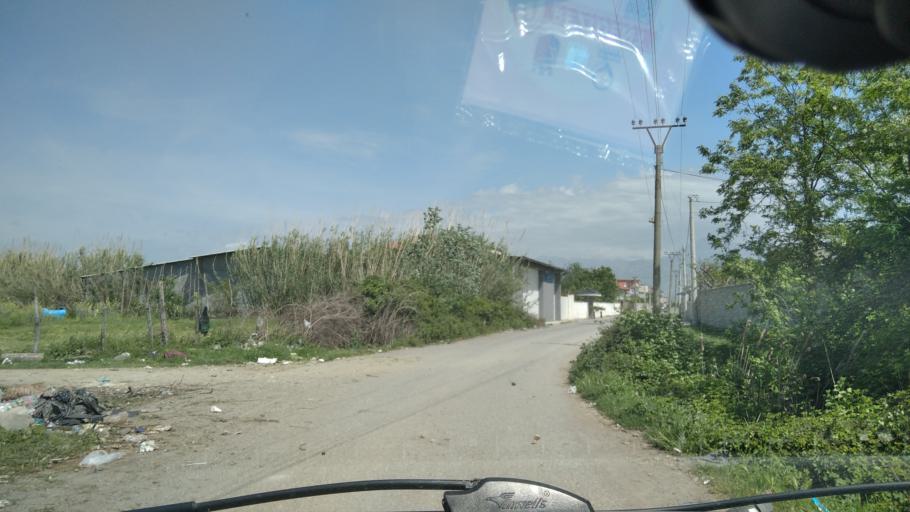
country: AL
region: Shkoder
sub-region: Rrethi i Malesia e Madhe
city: Kuc
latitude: 42.0506
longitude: 19.5212
